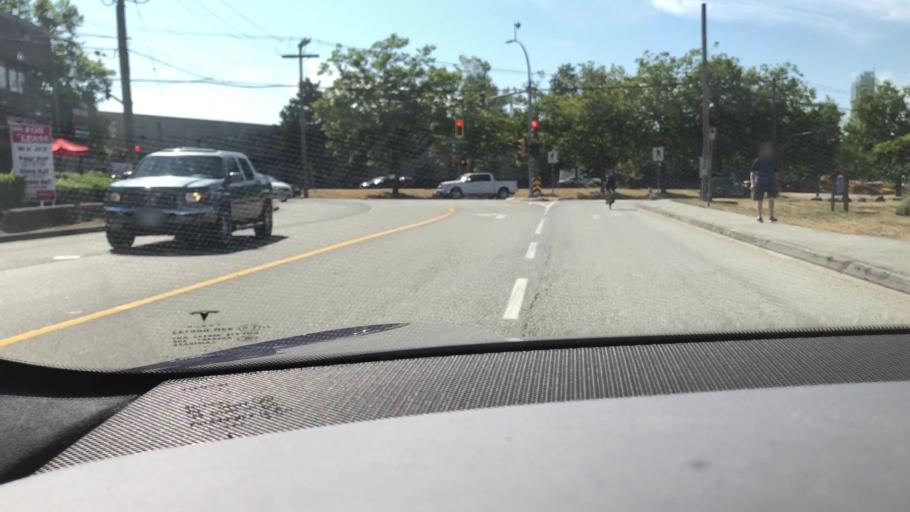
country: CA
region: British Columbia
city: Burnaby
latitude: 49.2593
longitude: -122.9825
